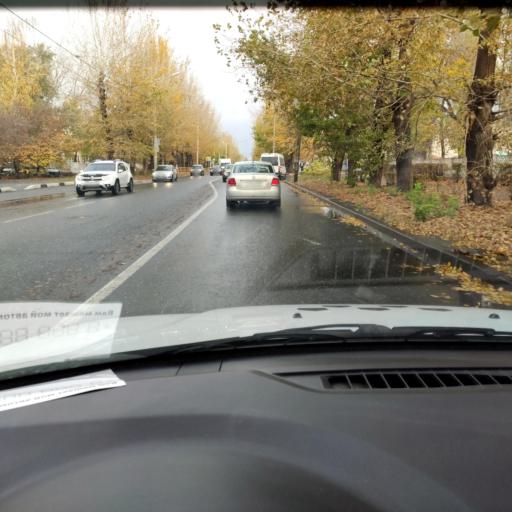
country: RU
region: Samara
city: Tol'yatti
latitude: 53.5336
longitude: 49.4113
